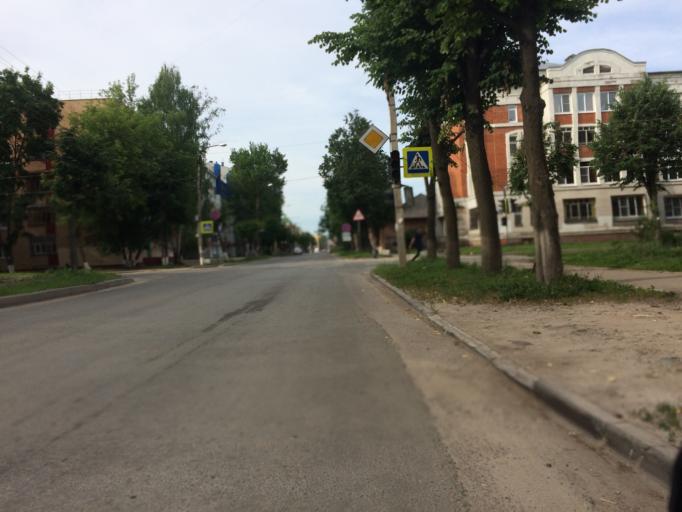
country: RU
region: Mariy-El
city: Yoshkar-Ola
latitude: 56.6420
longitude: 47.9023
